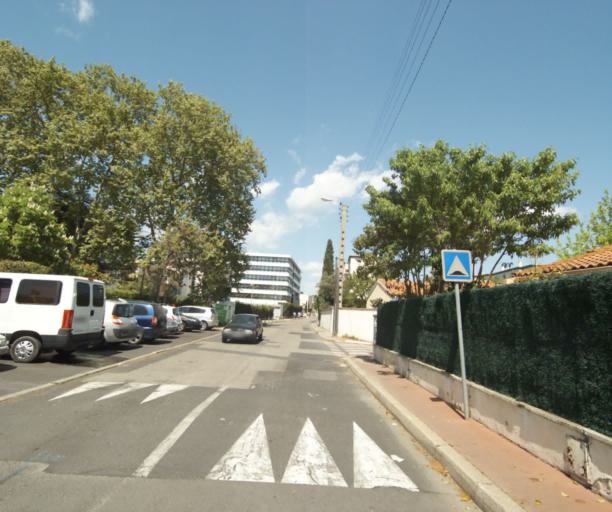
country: FR
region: Languedoc-Roussillon
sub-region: Departement de l'Herault
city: Juvignac
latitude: 43.6131
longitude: 3.8327
